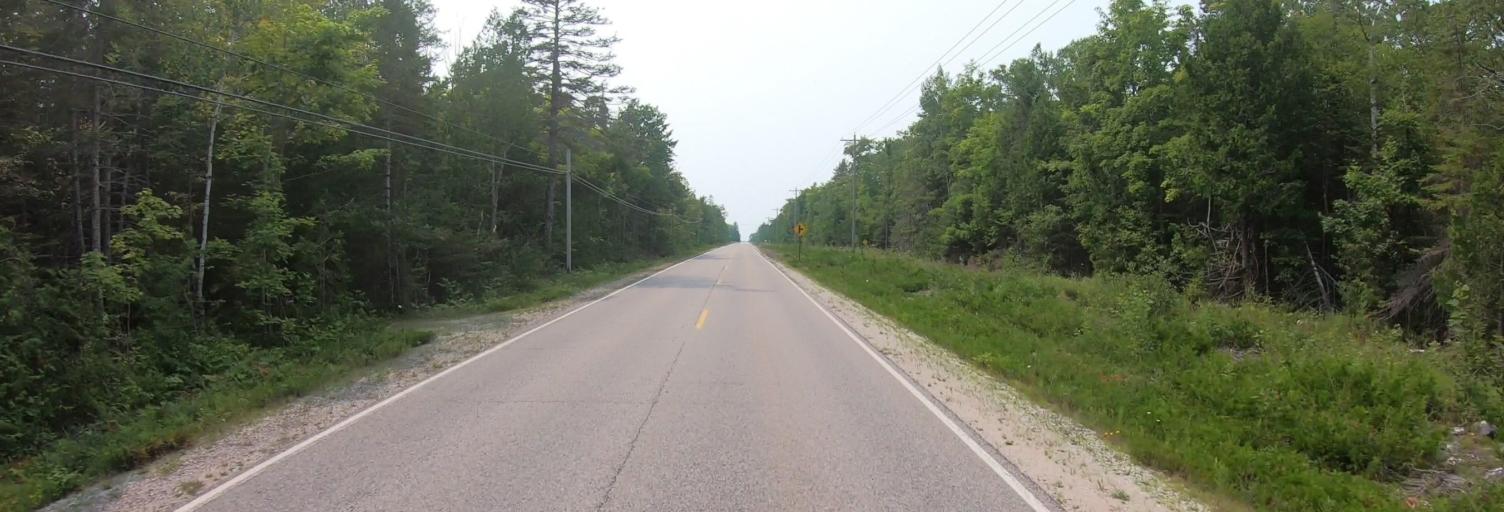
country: CA
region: Ontario
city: Thessalon
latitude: 46.0001
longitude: -83.9438
